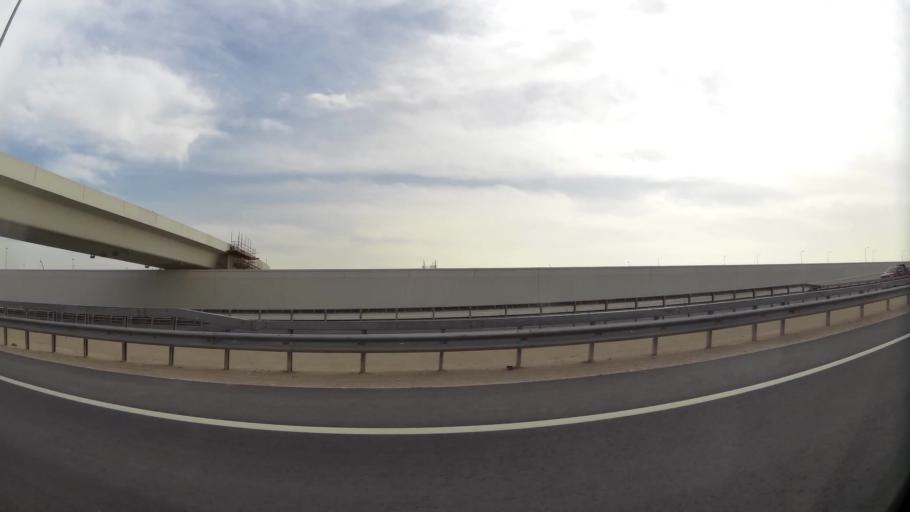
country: QA
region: Baladiyat ar Rayyan
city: Ar Rayyan
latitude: 25.3219
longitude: 51.3502
